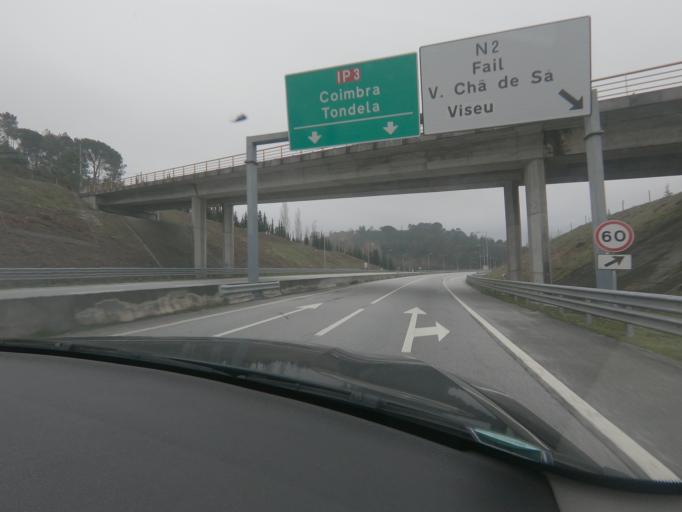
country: PT
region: Viseu
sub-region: Viseu
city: Viseu
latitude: 40.6157
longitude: -7.9635
